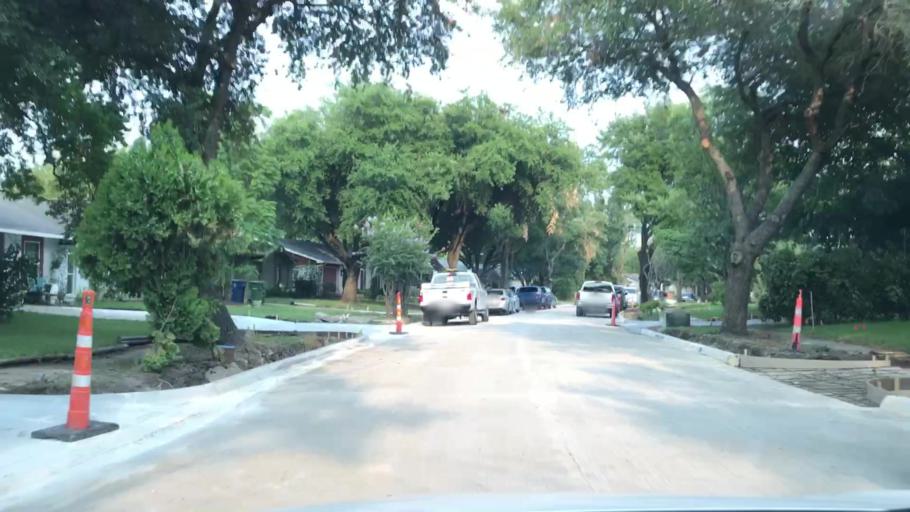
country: US
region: Texas
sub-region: Dallas County
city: Garland
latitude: 32.9278
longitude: -96.6110
